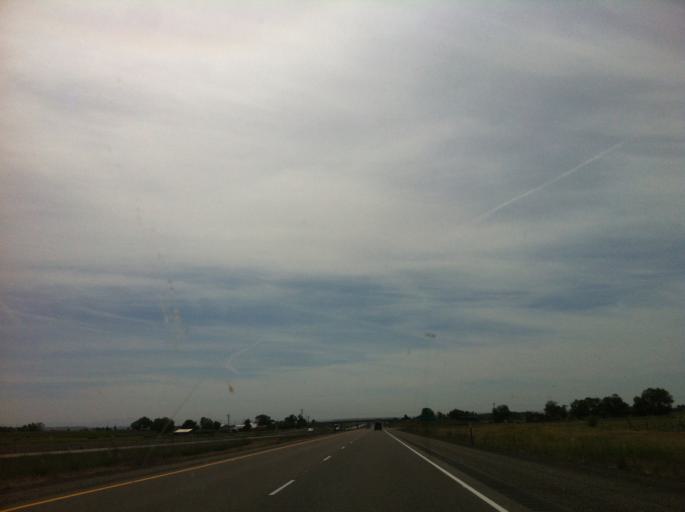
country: US
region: Oregon
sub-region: Malheur County
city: Ontario
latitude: 44.0881
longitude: -117.0236
